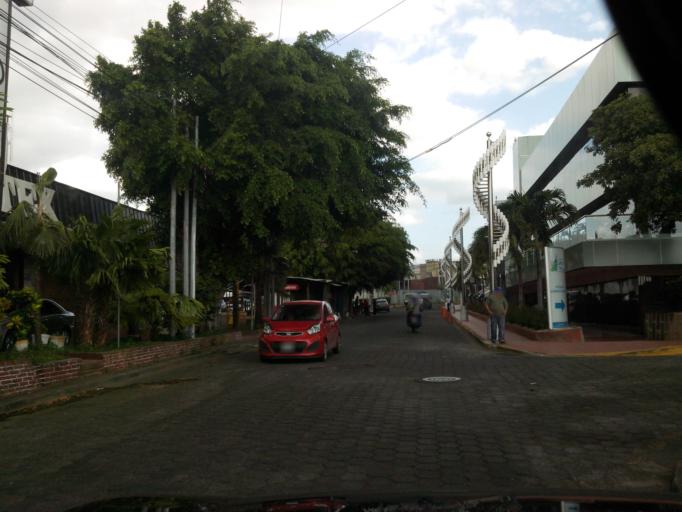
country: NI
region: Managua
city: Managua
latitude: 12.1162
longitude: -86.2562
